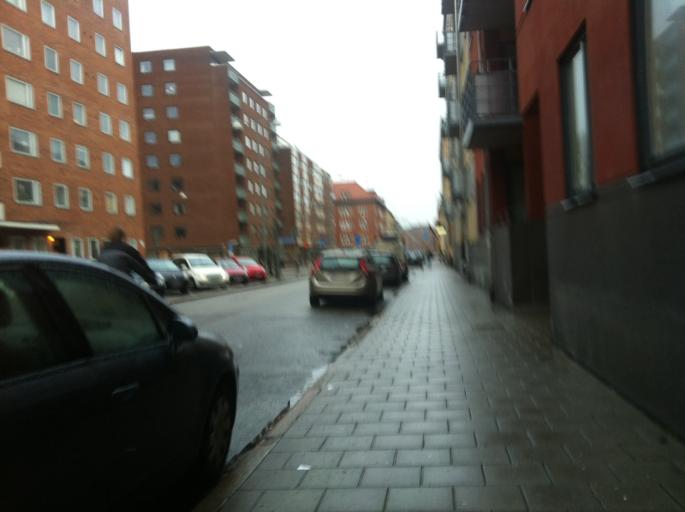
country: SE
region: Skane
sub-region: Malmo
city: Malmoe
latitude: 55.5936
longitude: 13.0065
